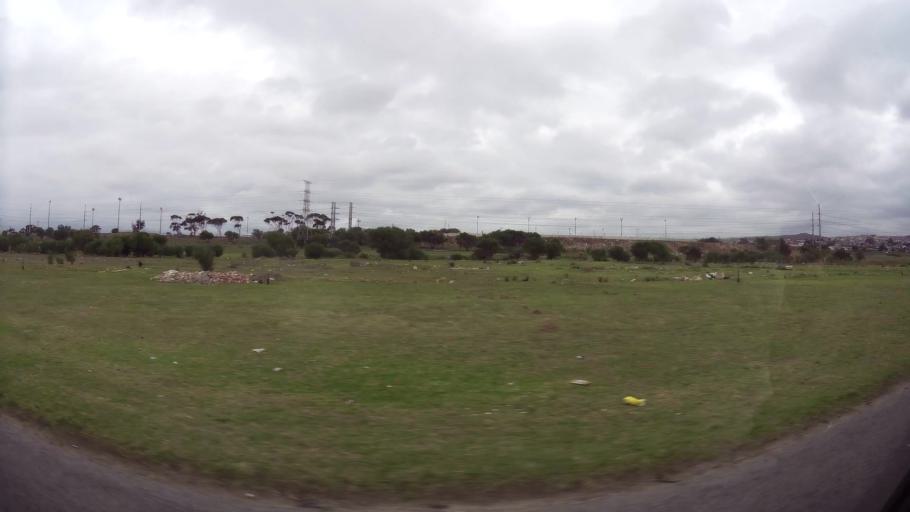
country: ZA
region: Eastern Cape
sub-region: Nelson Mandela Bay Metropolitan Municipality
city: Port Elizabeth
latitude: -33.9076
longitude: 25.5620
